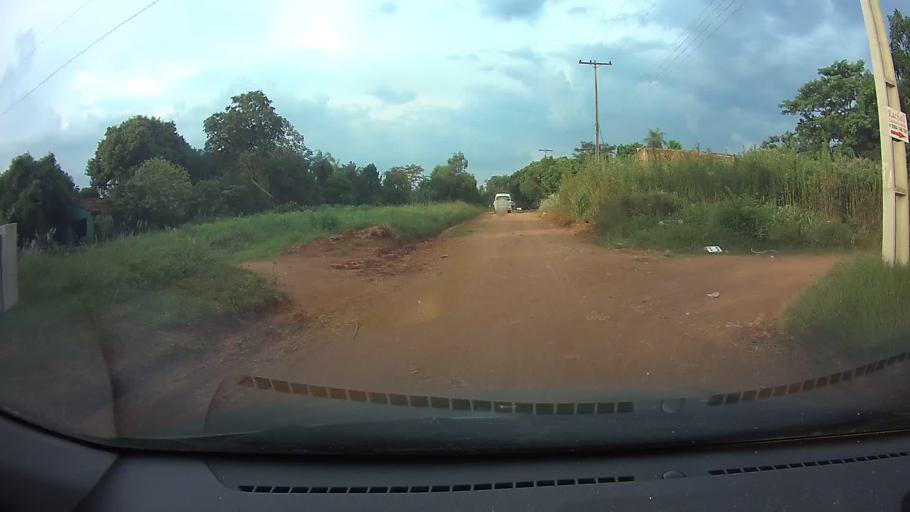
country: PY
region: Central
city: Limpio
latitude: -25.2439
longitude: -57.4547
